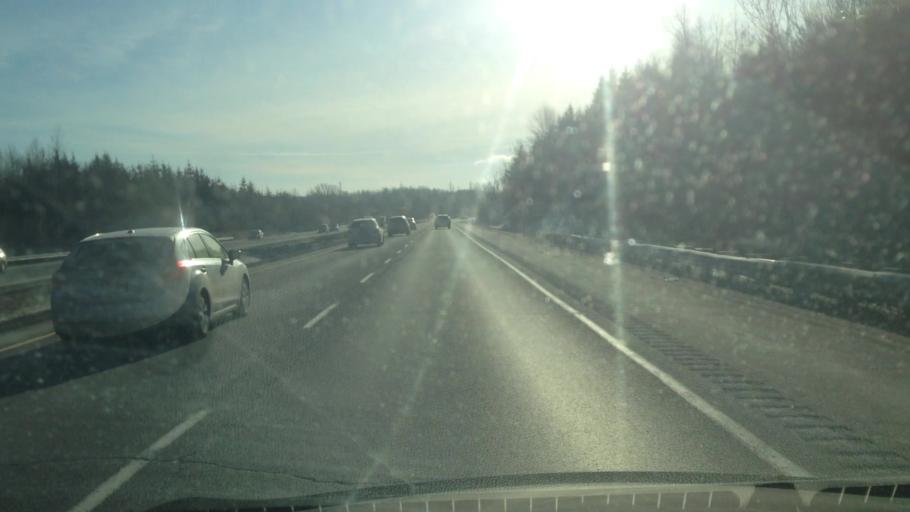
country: CA
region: Quebec
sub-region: Laurentides
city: Prevost
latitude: 45.8330
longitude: -74.0624
